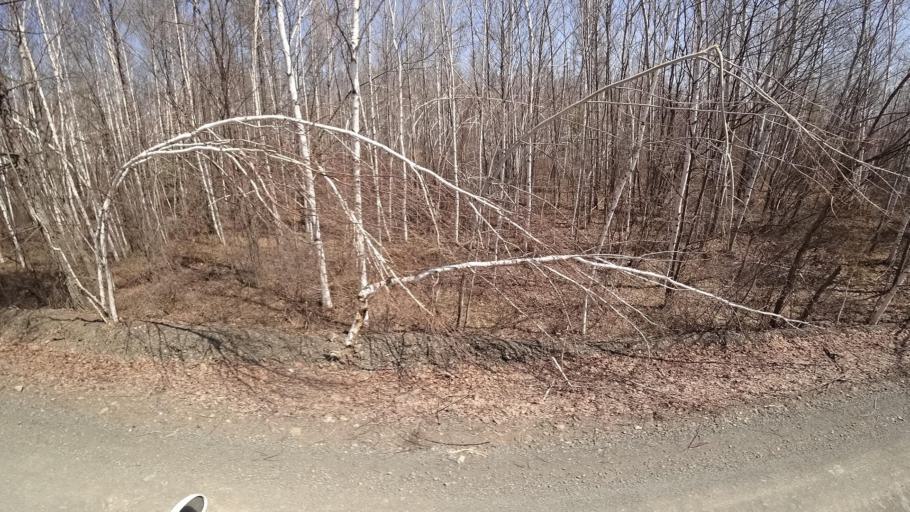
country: RU
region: Khabarovsk Krai
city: Khurba
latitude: 50.4121
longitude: 136.8432
